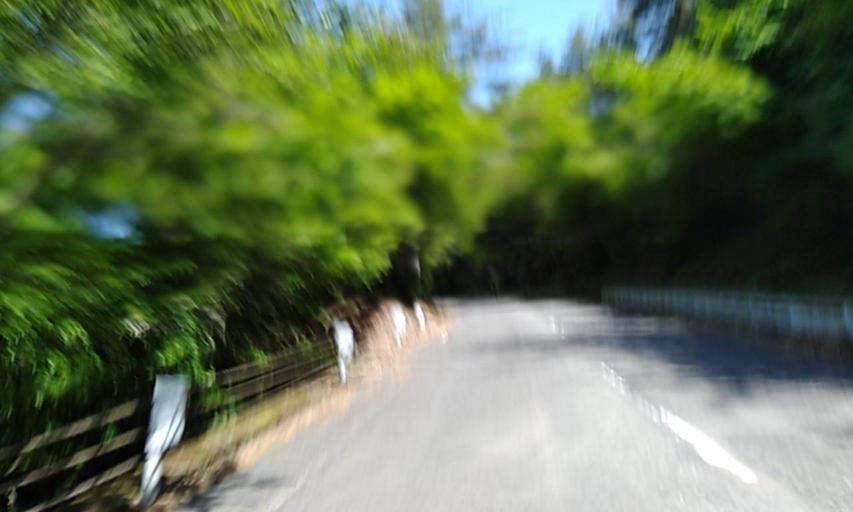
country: JP
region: Fukui
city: Obama
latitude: 35.5467
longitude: 135.7398
